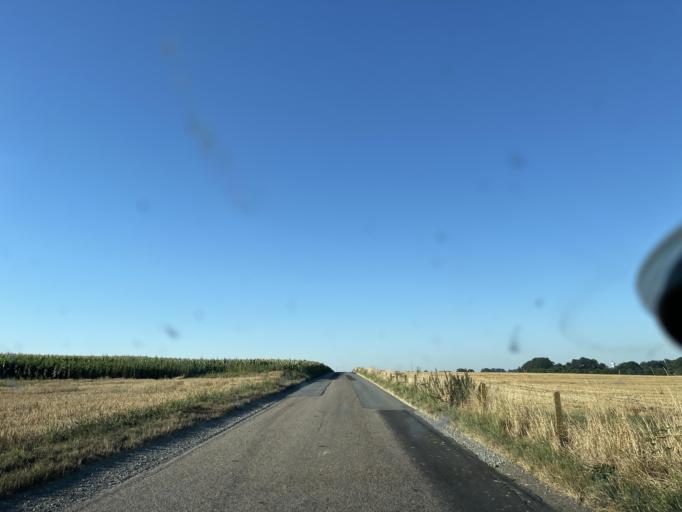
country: FR
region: Haute-Normandie
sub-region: Departement de la Seine-Maritime
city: Fauville-en-Caux
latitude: 49.6256
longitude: 0.6240
